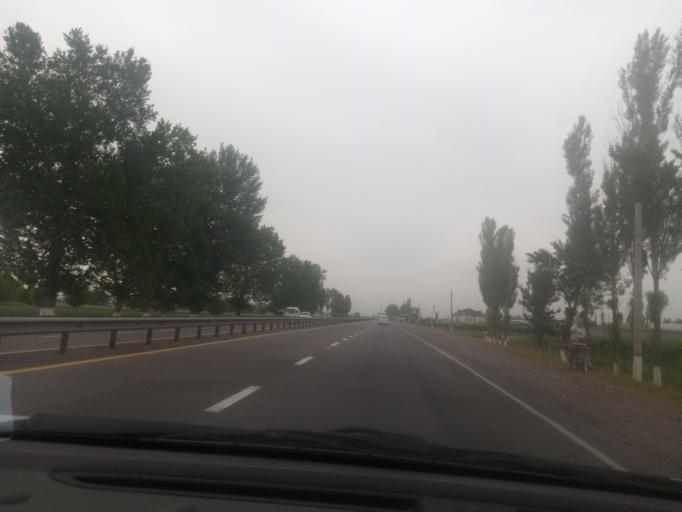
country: UZ
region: Toshkent Shahri
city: Bektemir
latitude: 41.1397
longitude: 69.4334
